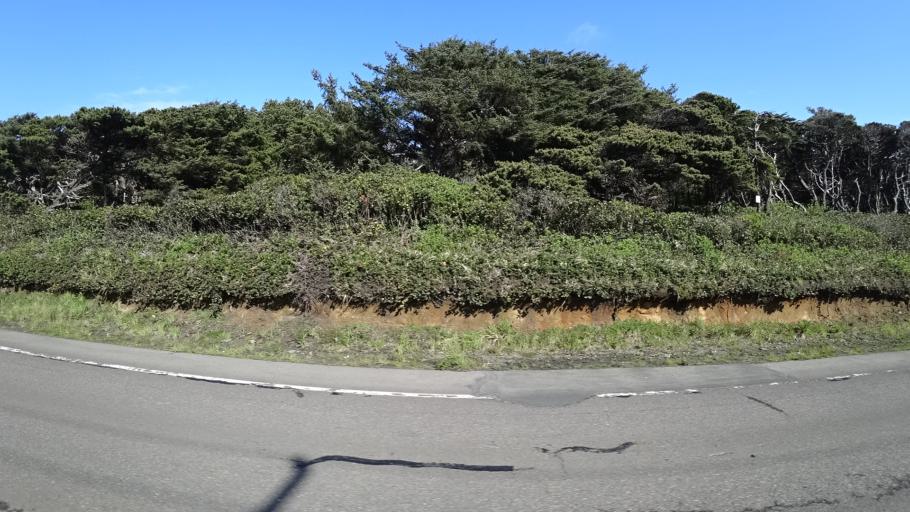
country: US
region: Oregon
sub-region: Lincoln County
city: Newport
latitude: 44.5567
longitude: -124.0714
